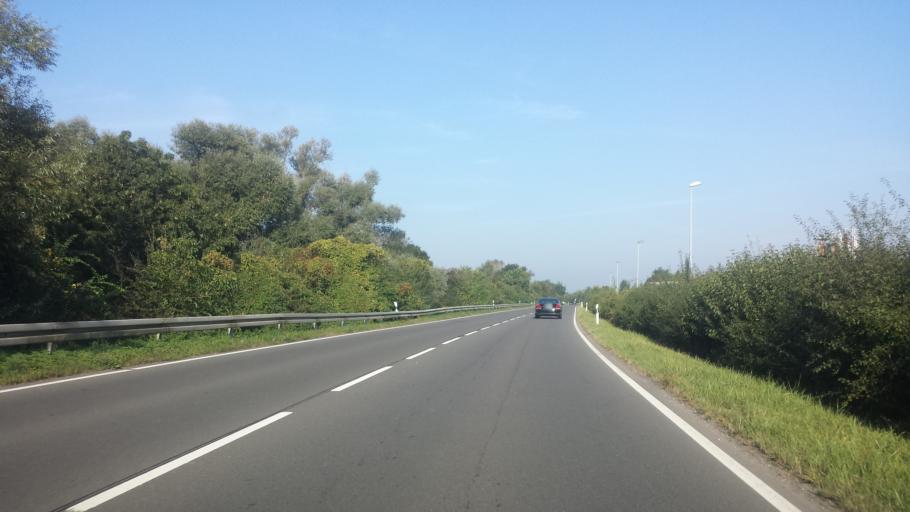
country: DE
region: Hesse
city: Lampertheim
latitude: 49.6076
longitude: 8.4515
